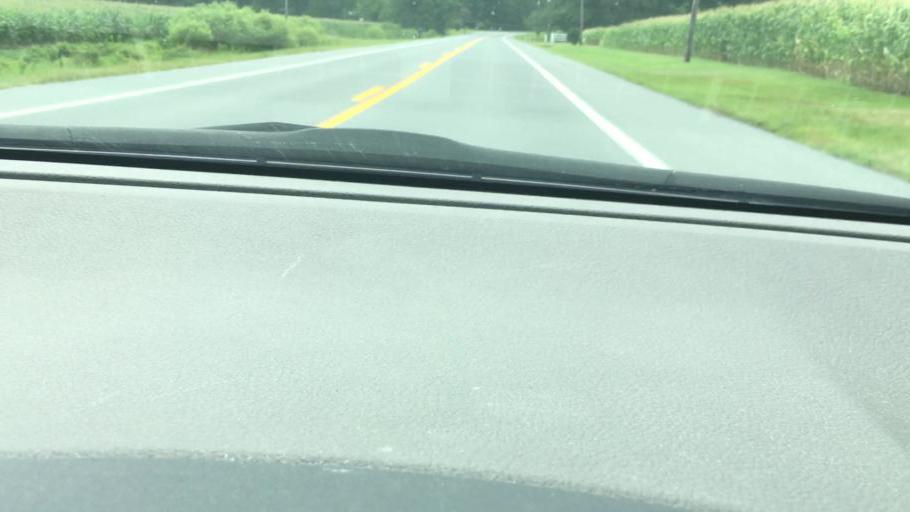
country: US
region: Maryland
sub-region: Worcester County
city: Pocomoke City
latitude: 38.0657
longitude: -75.5152
